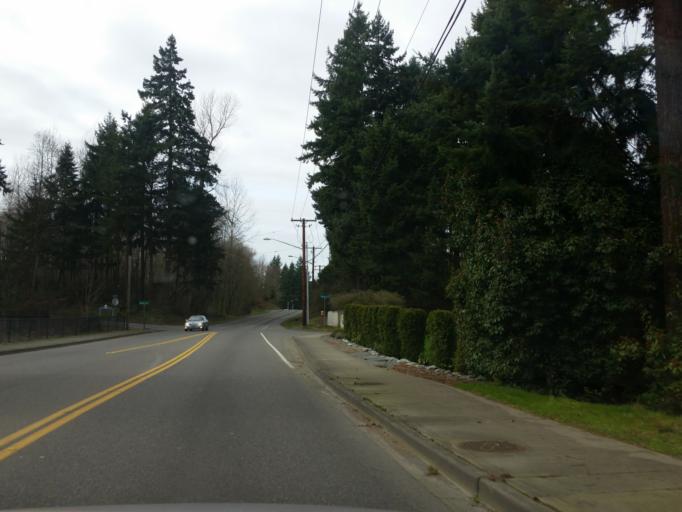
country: US
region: Washington
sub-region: Pierce County
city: South Hill
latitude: 47.1456
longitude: -122.2539
